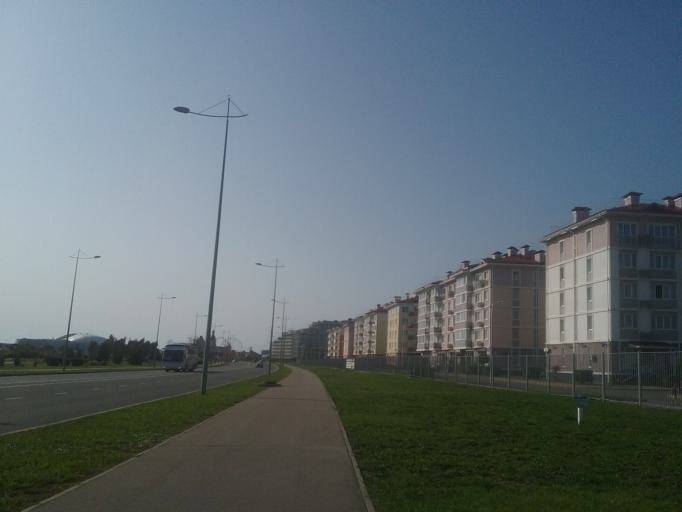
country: RU
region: Krasnodarskiy
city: Adler
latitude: 43.3992
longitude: 39.9816
